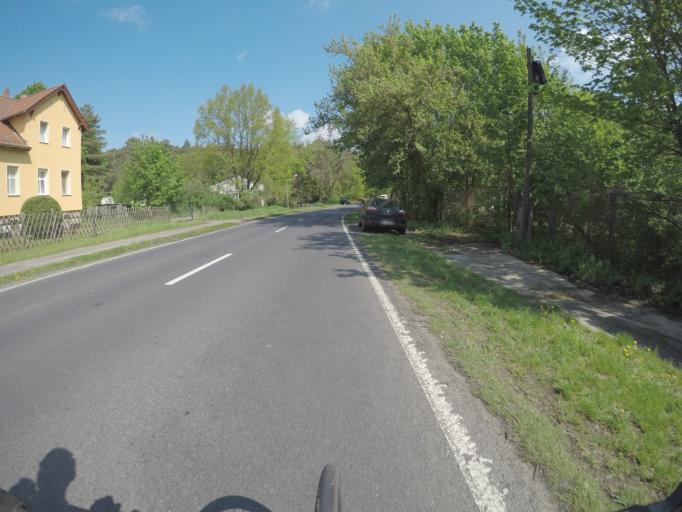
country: DE
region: Brandenburg
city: Marienwerder
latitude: 52.7941
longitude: 13.5487
